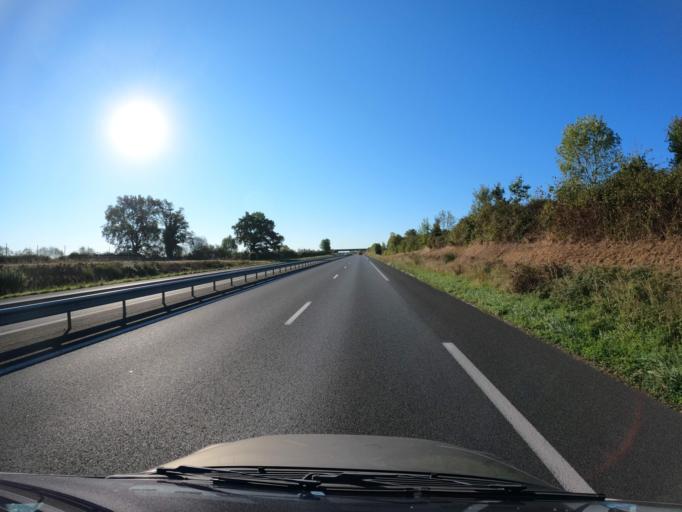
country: FR
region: Pays de la Loire
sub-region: Departement de Maine-et-Loire
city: La Tessoualle
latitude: 47.0070
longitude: -0.8685
